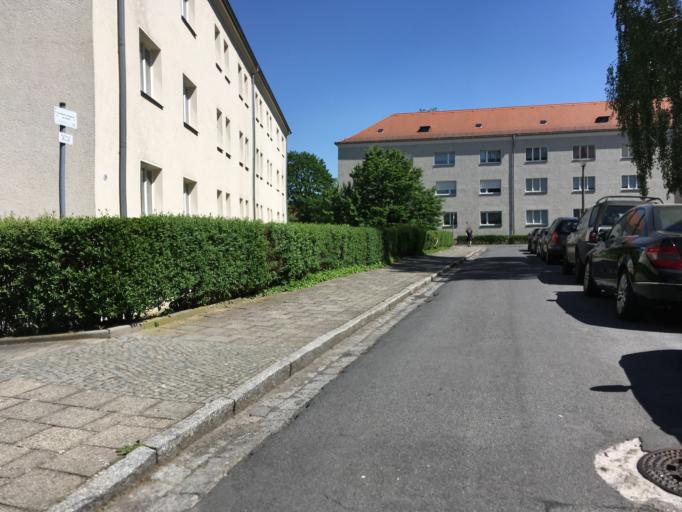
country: DE
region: Saxony
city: Radebeul
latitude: 51.0947
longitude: 13.7083
